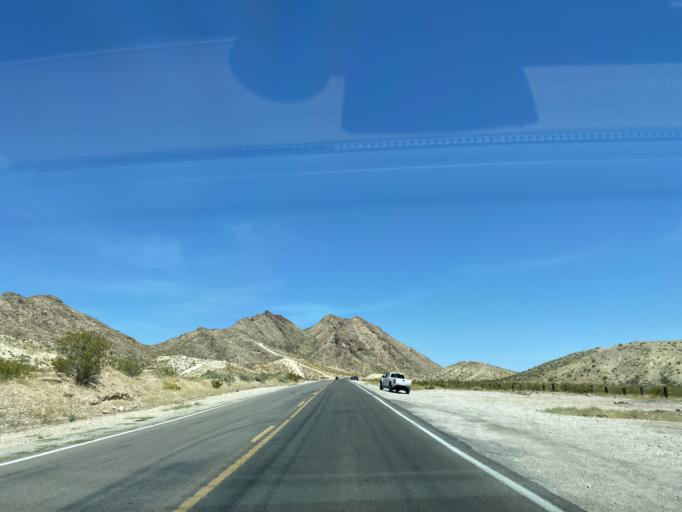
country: US
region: Nevada
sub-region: Clark County
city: Nellis Air Force Base
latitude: 36.2014
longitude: -114.9923
